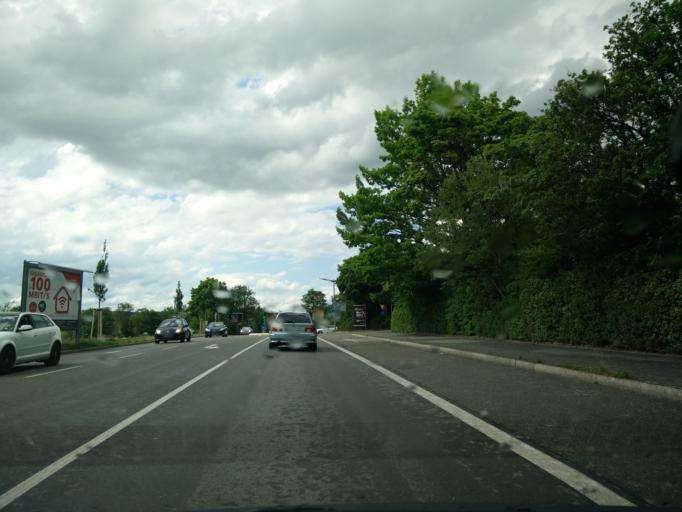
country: DE
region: Baden-Wuerttemberg
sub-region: Freiburg Region
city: Bad Durrheim
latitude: 48.0499
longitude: 8.5342
